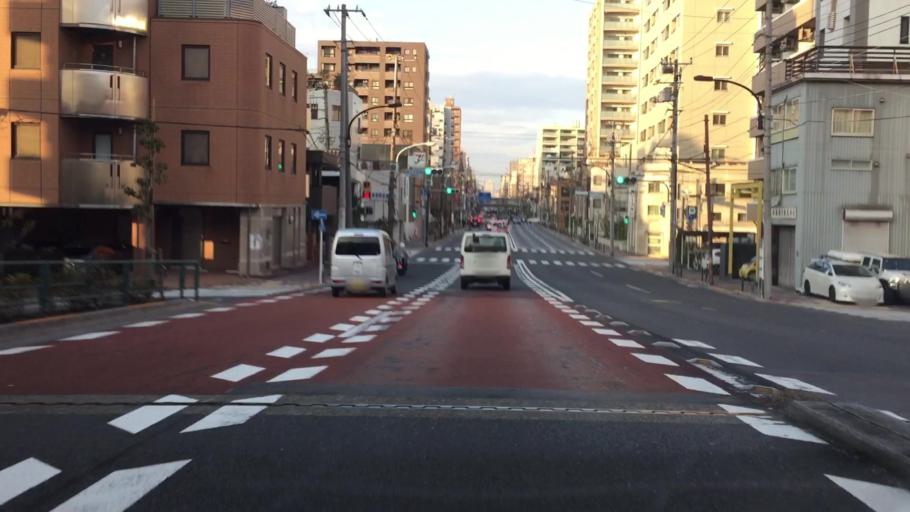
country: JP
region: Tokyo
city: Urayasu
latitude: 35.6927
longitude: 139.8057
